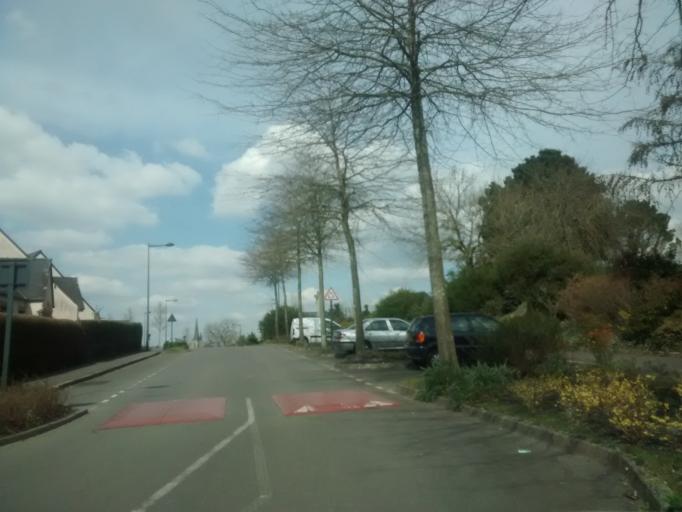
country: FR
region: Brittany
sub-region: Departement d'Ille-et-Vilaine
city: Chantepie
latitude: 48.0850
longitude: -1.6137
